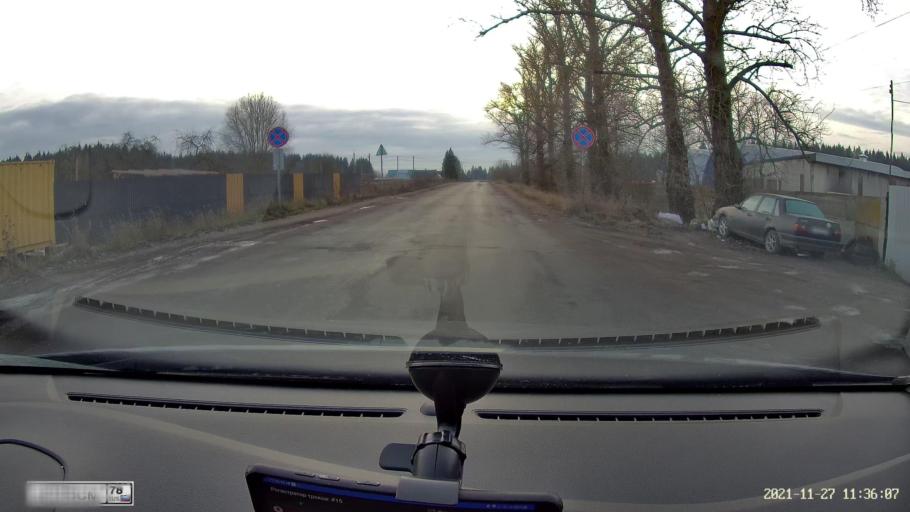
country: RU
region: Leningrad
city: Russko-Vysotskoye
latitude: 59.7011
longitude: 29.9776
